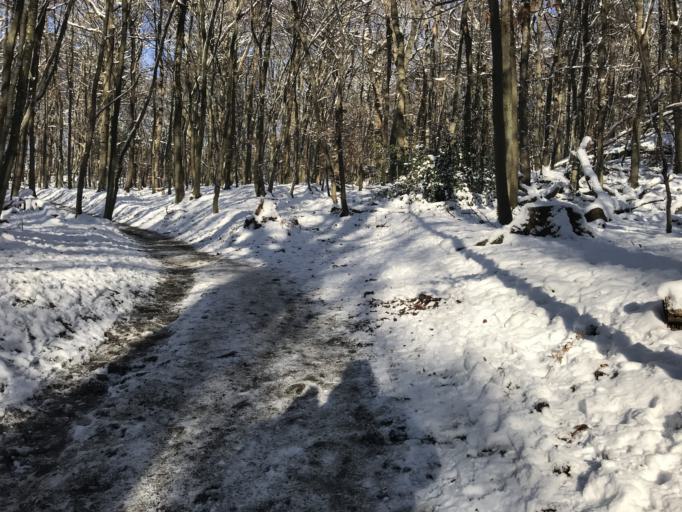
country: DE
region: Hesse
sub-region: Regierungsbezirk Darmstadt
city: Konigstein im Taunus
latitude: 50.1857
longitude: 8.4742
